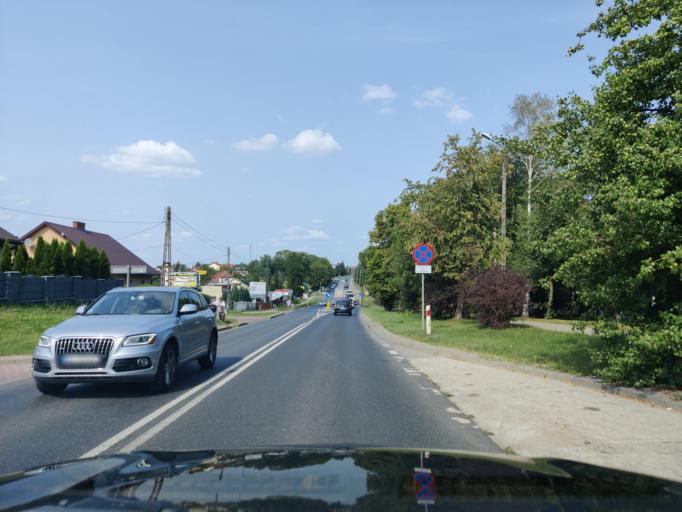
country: PL
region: Masovian Voivodeship
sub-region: Powiat pultuski
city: Pultusk
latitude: 52.7151
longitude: 21.0840
